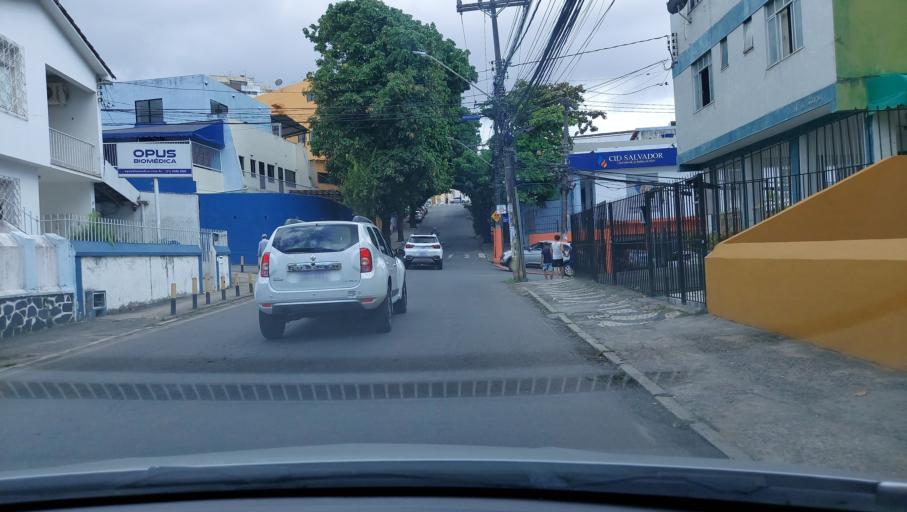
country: BR
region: Bahia
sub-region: Salvador
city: Salvador
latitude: -12.9725
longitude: -38.4906
